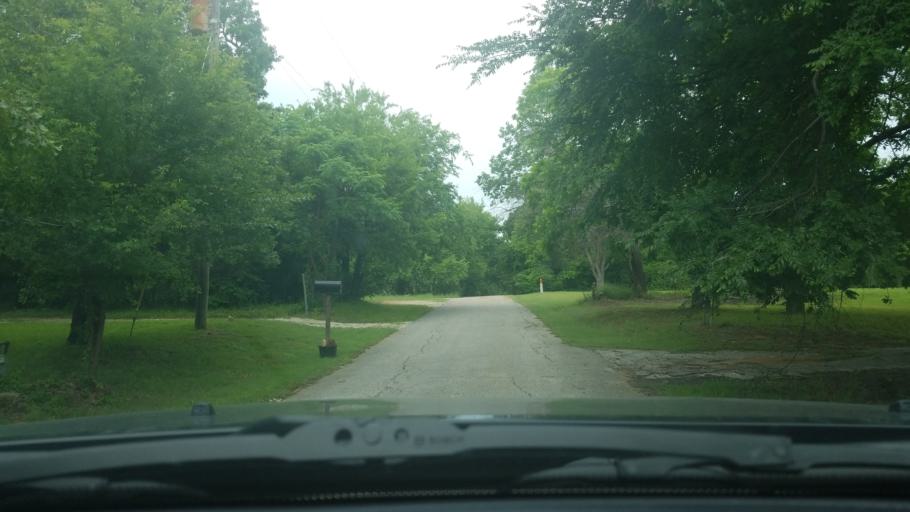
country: US
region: Texas
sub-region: Denton County
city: Lake Dallas
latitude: 33.1151
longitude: -97.0171
